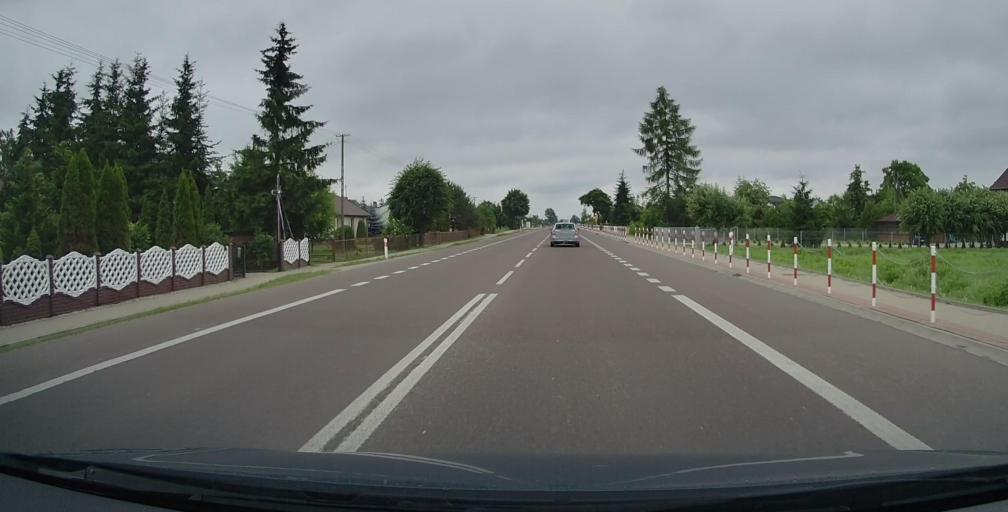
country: PL
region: Lublin Voivodeship
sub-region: Powiat bialski
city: Rzeczyca
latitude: 52.0343
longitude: 22.6997
